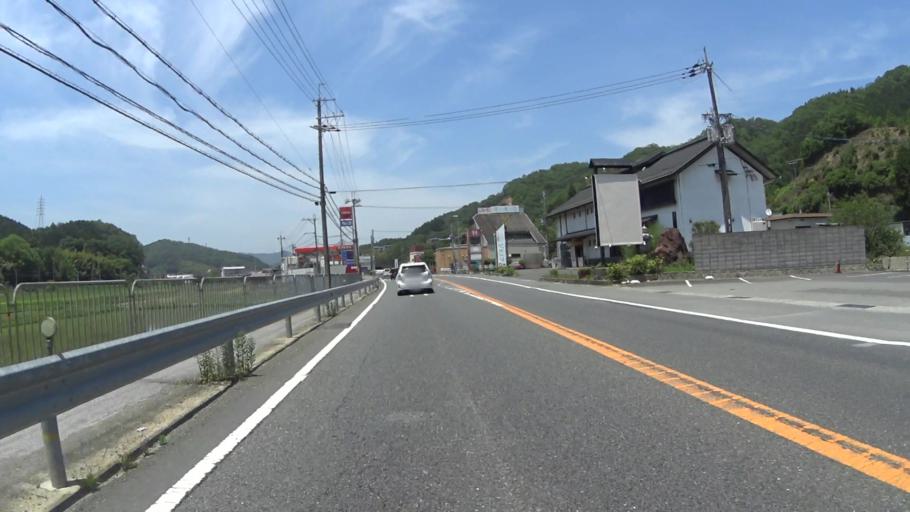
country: JP
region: Kyoto
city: Kameoka
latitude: 35.0980
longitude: 135.4941
